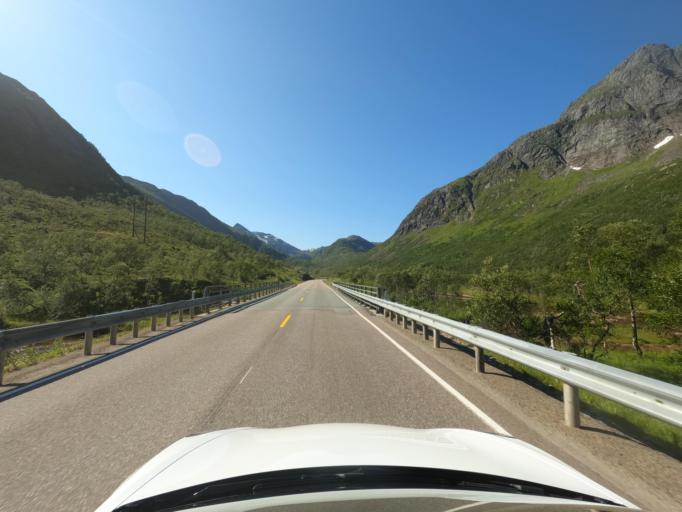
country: NO
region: Nordland
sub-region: Lodingen
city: Lodingen
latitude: 68.5026
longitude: 15.7097
